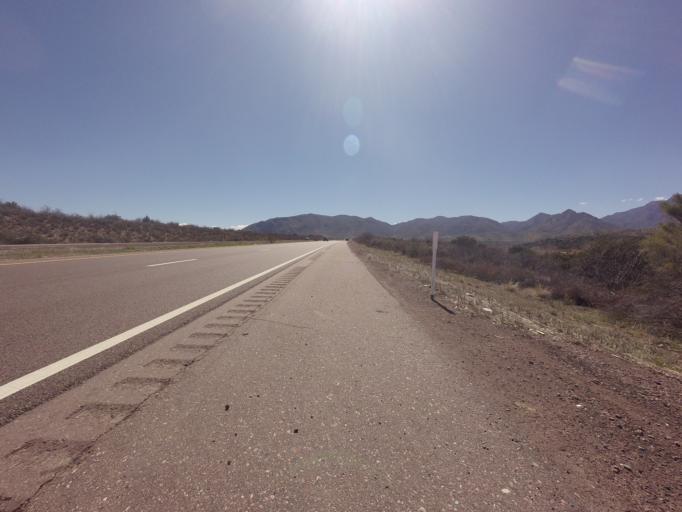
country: US
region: Arizona
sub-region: Gila County
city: Payson
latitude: 34.0575
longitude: -111.3633
